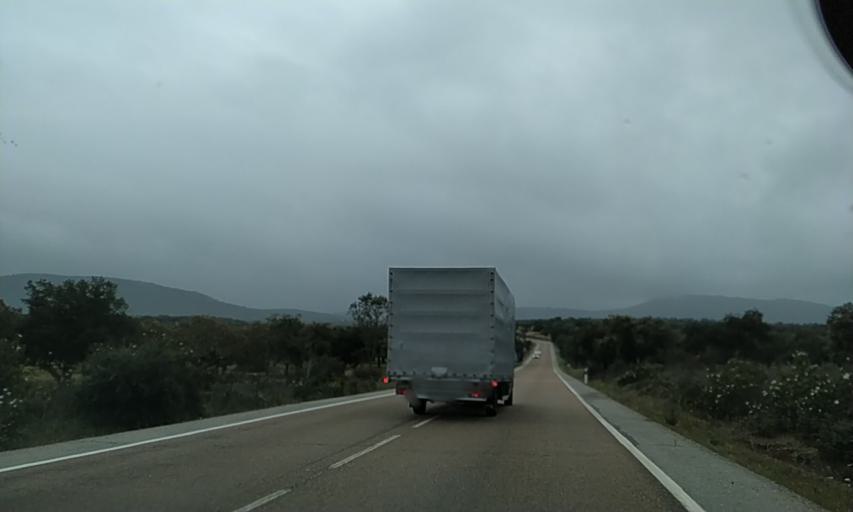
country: ES
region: Extremadura
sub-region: Provincia de Badajoz
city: Puebla de Obando
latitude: 39.2182
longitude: -6.5794
